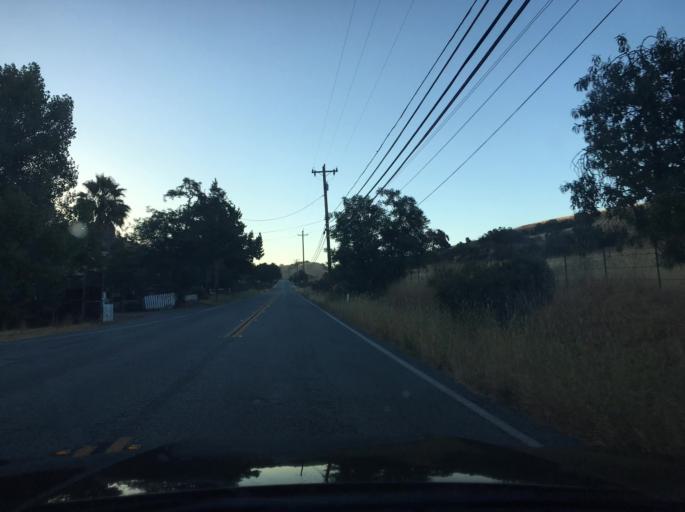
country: US
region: California
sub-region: Santa Clara County
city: Seven Trees
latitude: 37.1881
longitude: -121.7852
